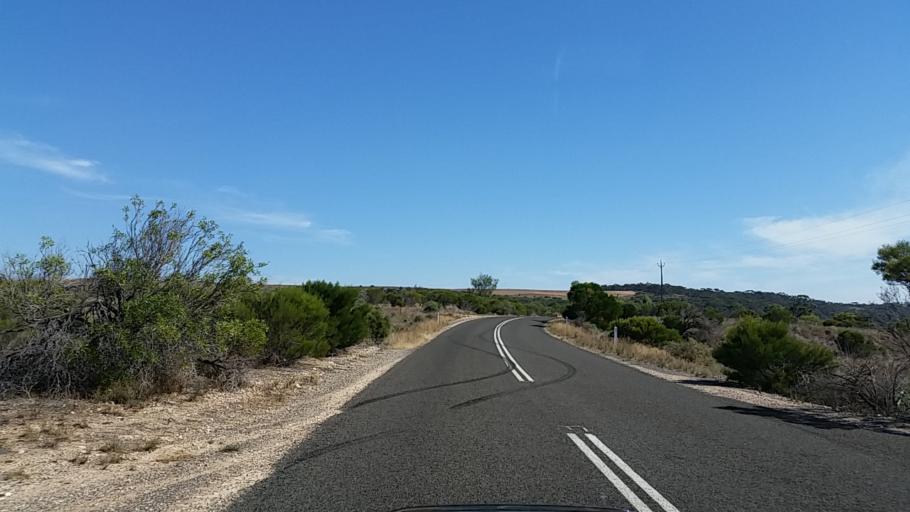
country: AU
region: South Australia
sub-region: Mid Murray
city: Mannum
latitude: -34.7471
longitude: 139.5435
